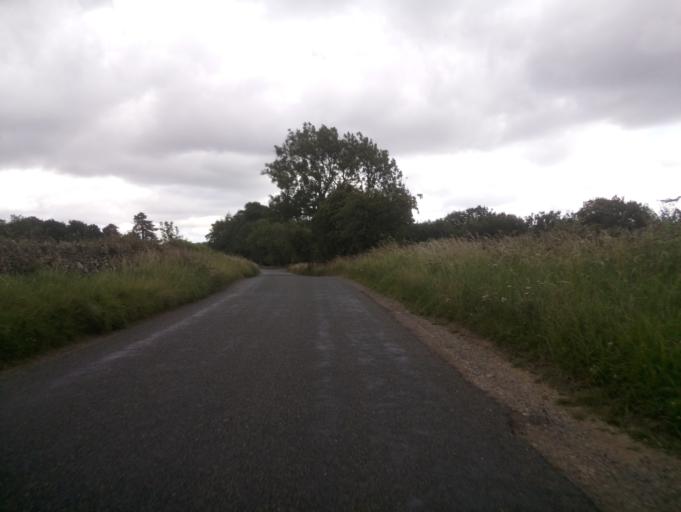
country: GB
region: England
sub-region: Gloucestershire
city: Chalford
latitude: 51.7850
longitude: -2.1109
